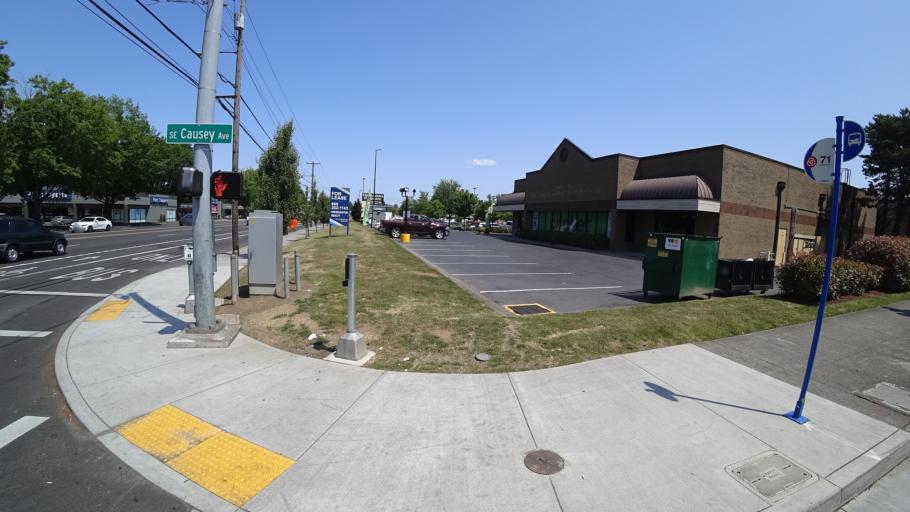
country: US
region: Oregon
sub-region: Clackamas County
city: Oatfield
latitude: 45.4414
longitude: -122.5787
